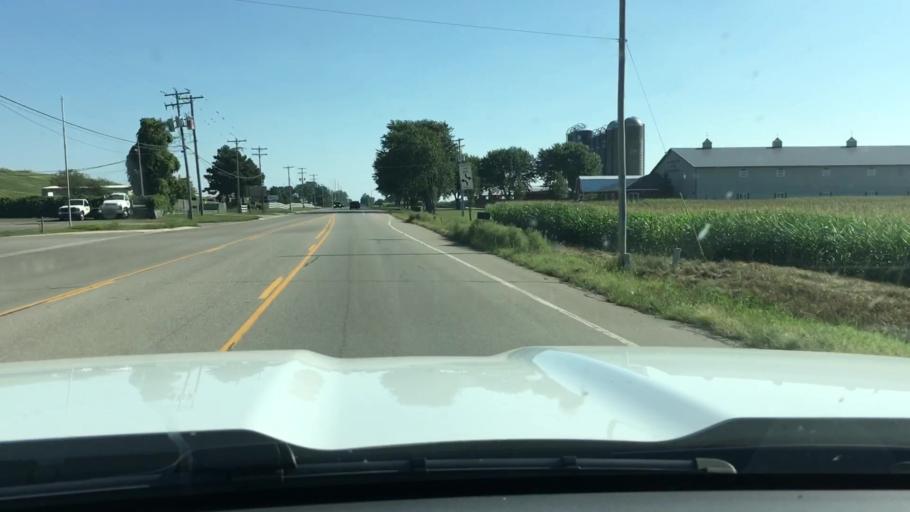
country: US
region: Michigan
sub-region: Ottawa County
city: Coopersville
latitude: 43.0536
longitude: -85.9569
